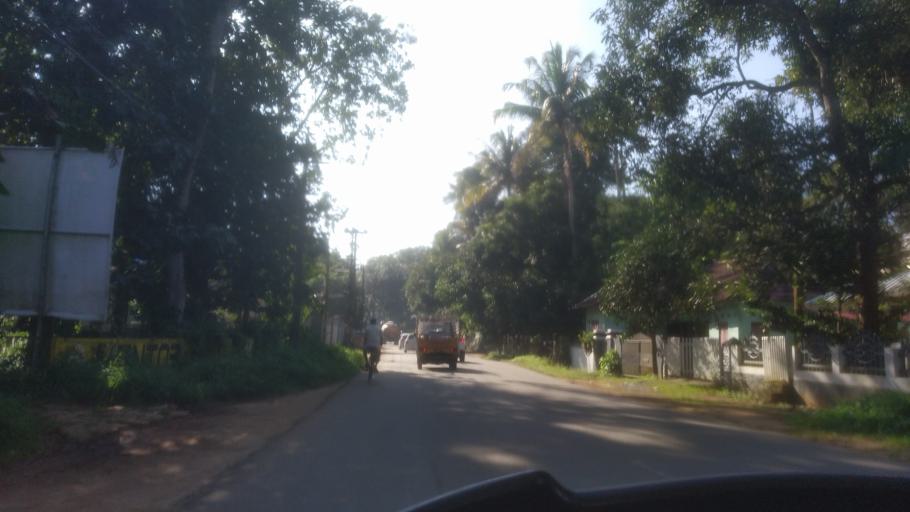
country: IN
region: Kerala
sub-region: Ernakulam
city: Muvattupuzha
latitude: 9.9763
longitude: 76.5318
